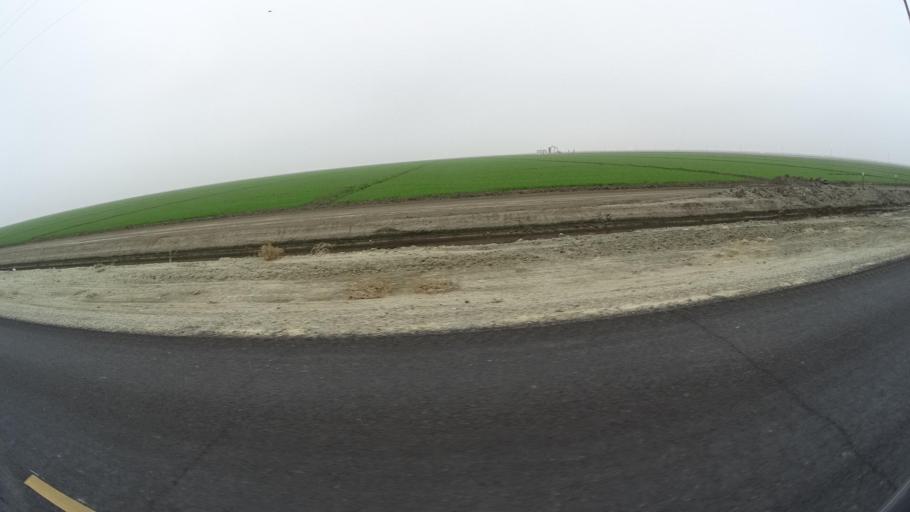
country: US
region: California
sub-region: Kern County
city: Greenfield
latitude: 35.1801
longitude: -119.1860
